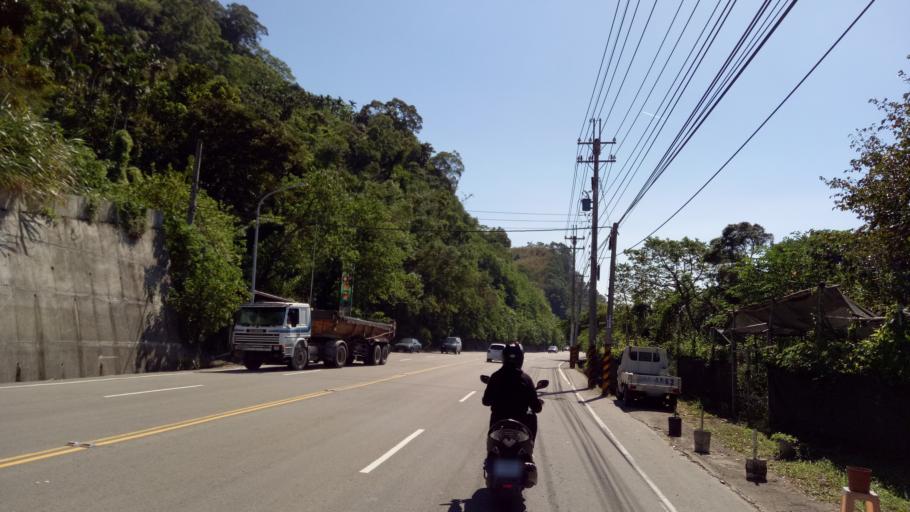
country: TW
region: Taiwan
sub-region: Hsinchu
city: Hsinchu
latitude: 24.6788
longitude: 120.9659
